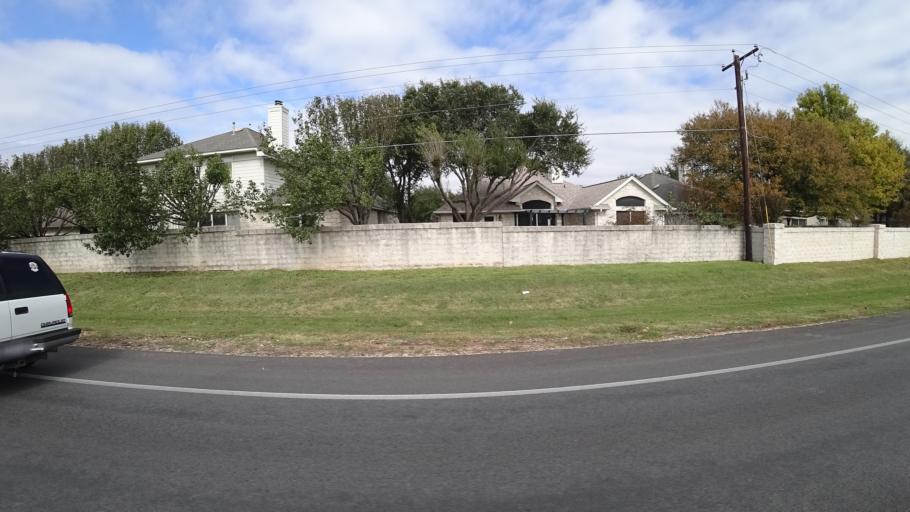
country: US
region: Texas
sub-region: Williamson County
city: Brushy Creek
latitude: 30.5320
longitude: -97.7086
